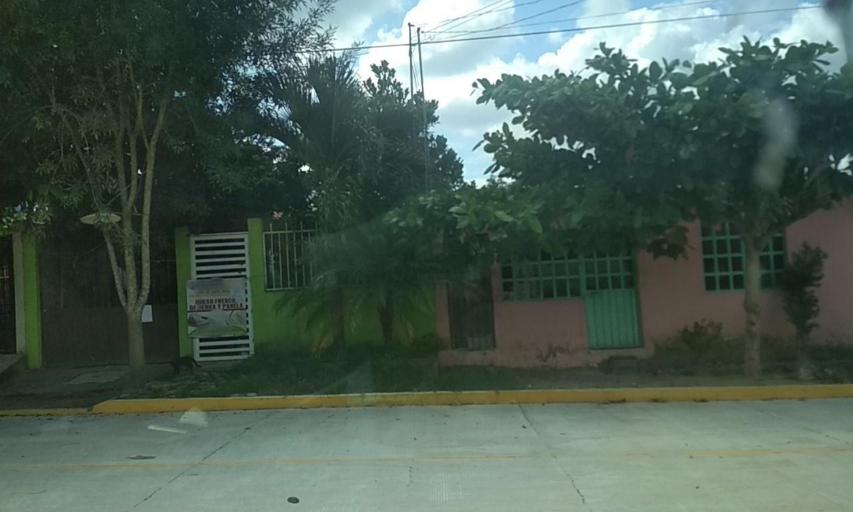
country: MX
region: Veracruz
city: Martinez de la Torre
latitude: 20.0773
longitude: -97.0790
